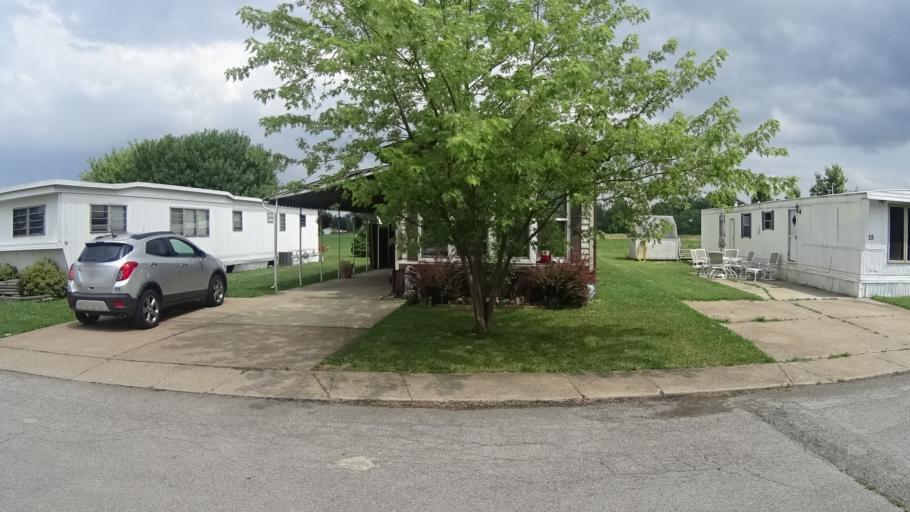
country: US
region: Ohio
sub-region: Erie County
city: Sandusky
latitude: 41.4384
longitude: -82.7574
